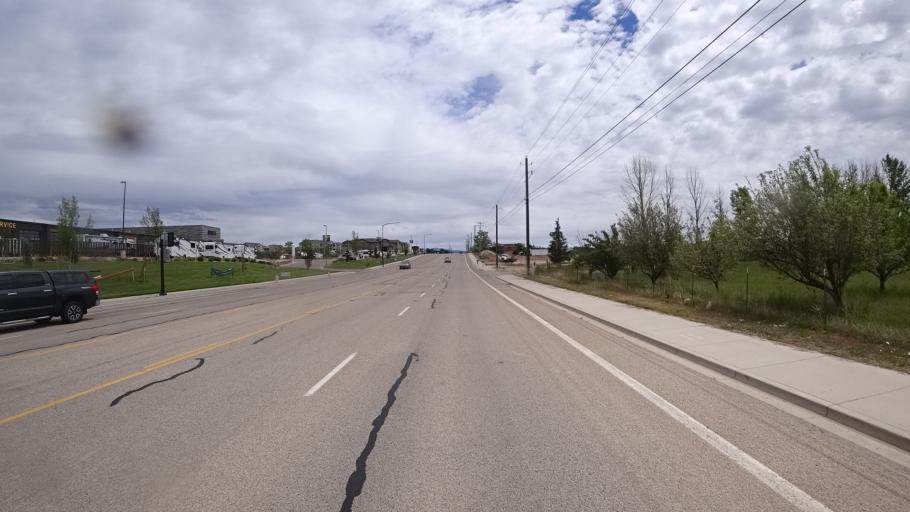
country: US
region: Idaho
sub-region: Ada County
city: Meridian
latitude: 43.5900
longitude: -116.4114
